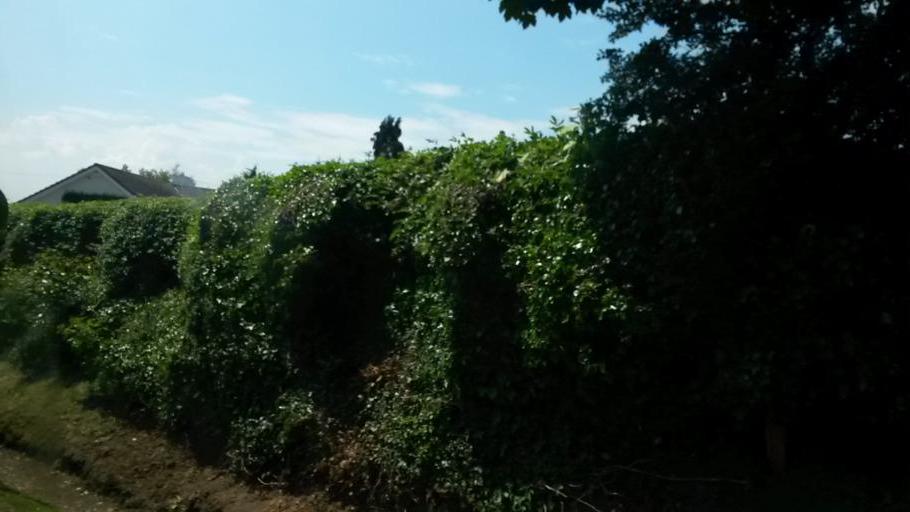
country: IE
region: Leinster
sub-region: An Mhi
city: Slane
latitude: 53.7146
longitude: -6.5392
